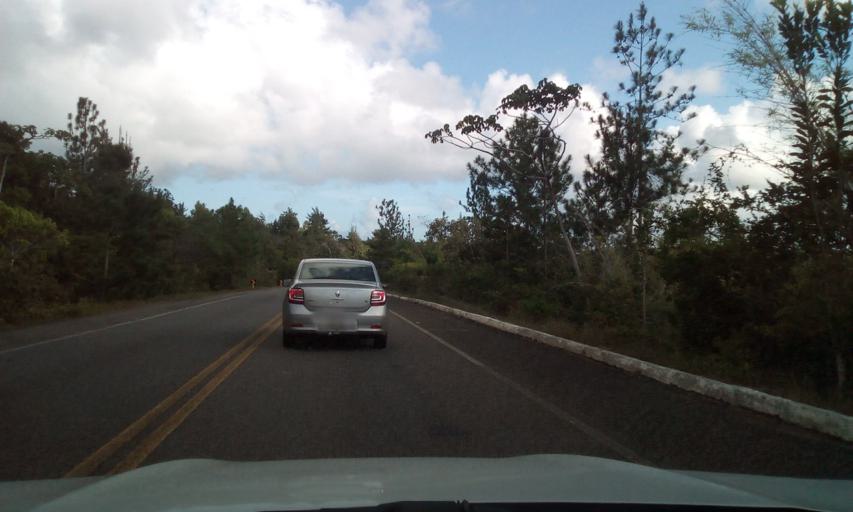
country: BR
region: Bahia
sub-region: Entre Rios
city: Entre Rios
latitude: -12.1320
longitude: -37.7919
